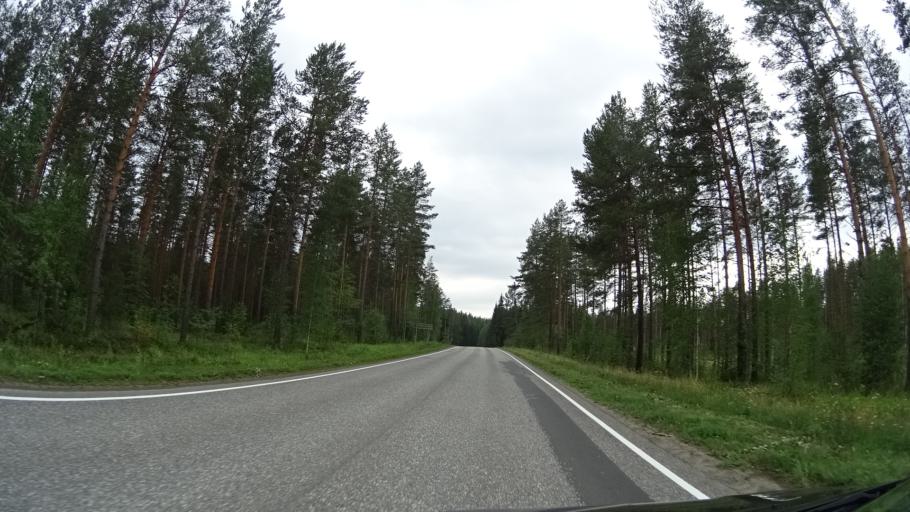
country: FI
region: Southern Savonia
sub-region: Savonlinna
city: Punkaharju
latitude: 61.7525
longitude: 29.4438
